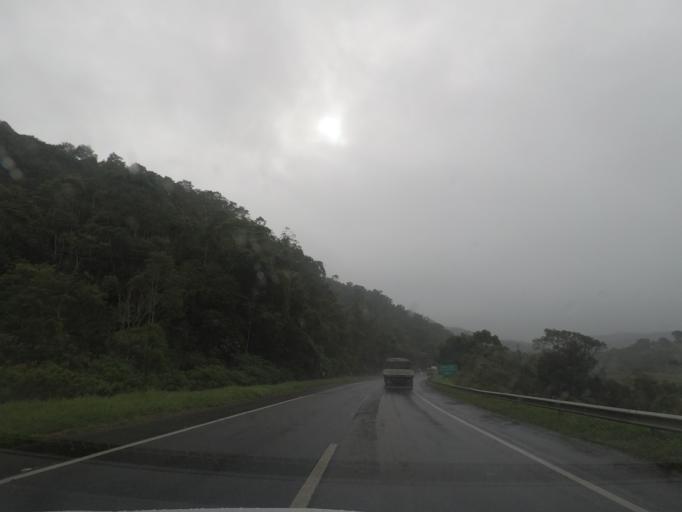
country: BR
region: Sao Paulo
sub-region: Cajati
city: Cajati
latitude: -24.9633
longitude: -48.4238
